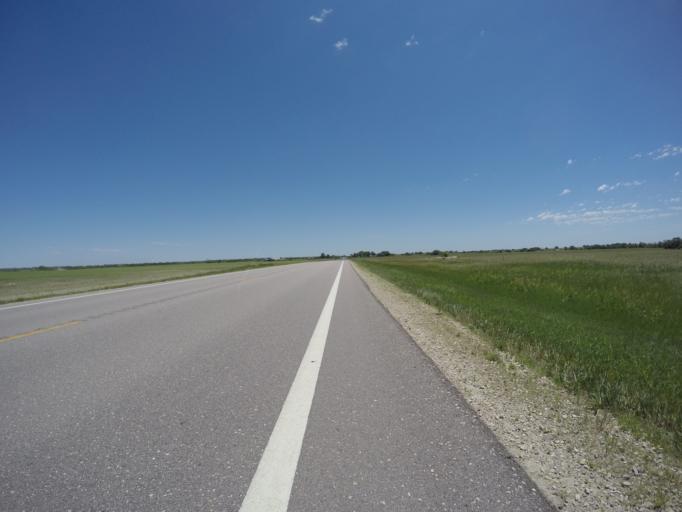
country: US
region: Kansas
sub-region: Republic County
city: Belleville
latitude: 39.8127
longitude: -97.6672
